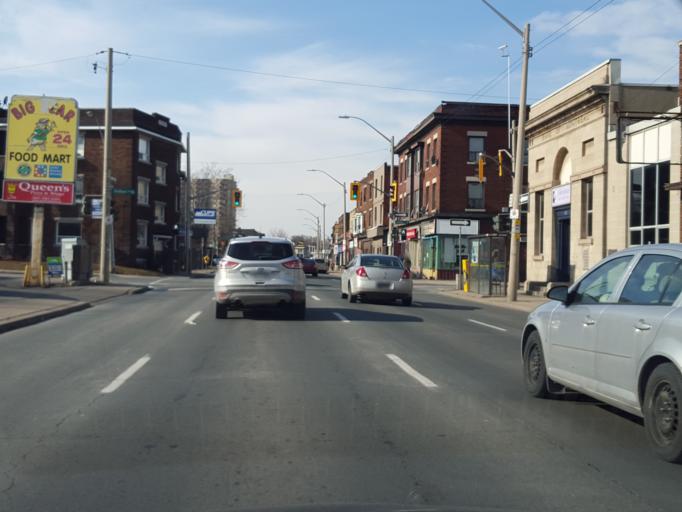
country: CA
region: Ontario
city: Hamilton
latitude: 43.2513
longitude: -79.8410
